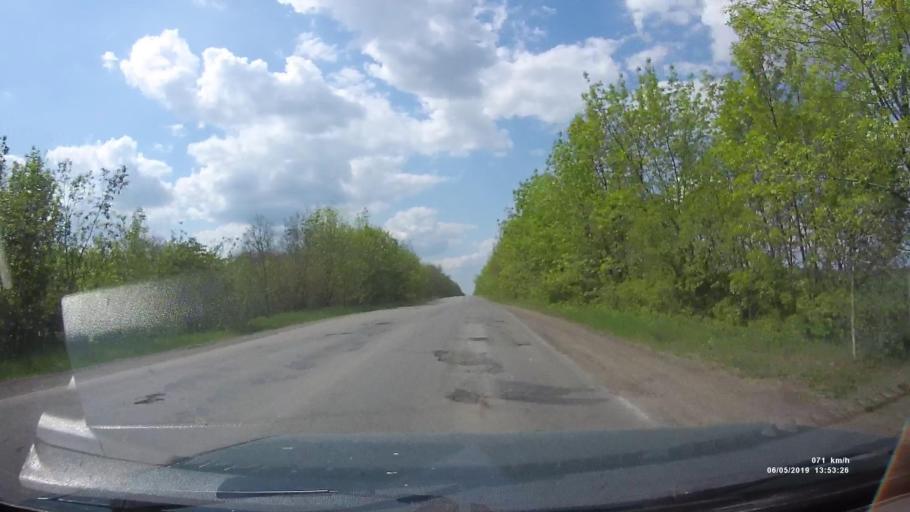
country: RU
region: Rostov
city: Melikhovskaya
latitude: 47.6682
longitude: 40.4625
